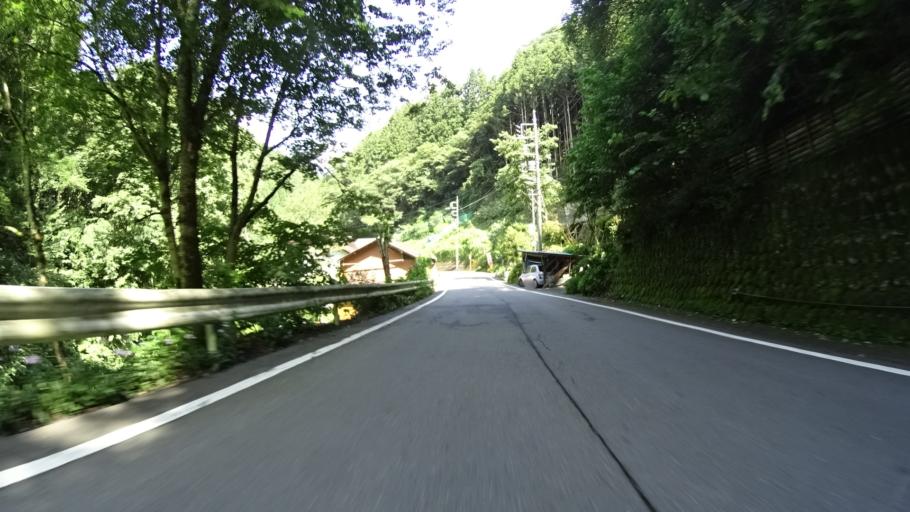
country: JP
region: Gunma
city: Tomioka
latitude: 36.0660
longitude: 138.8318
